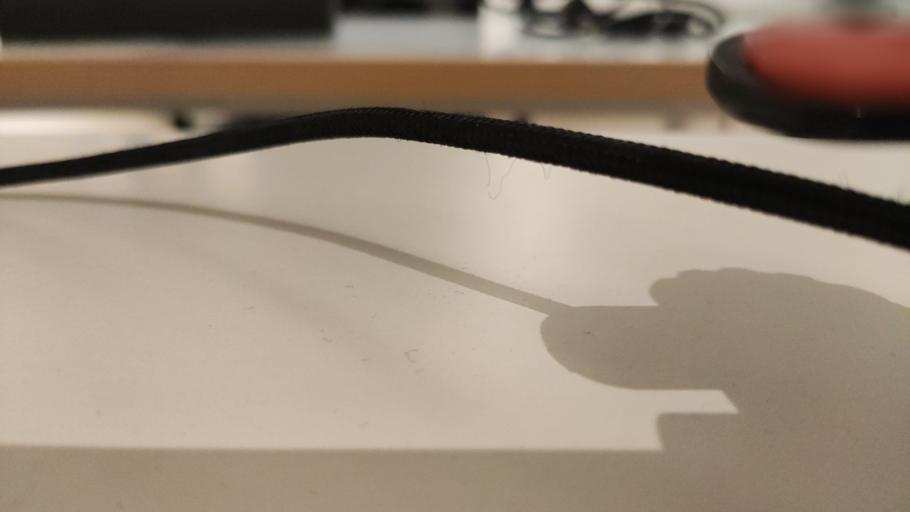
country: RU
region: Kaluga
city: Zhukovo
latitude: 55.1392
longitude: 36.7818
